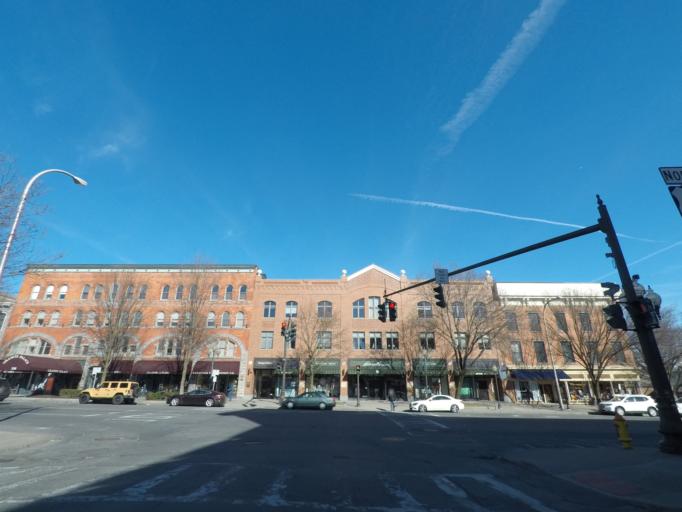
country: US
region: New York
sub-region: Saratoga County
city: Saratoga Springs
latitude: 43.0801
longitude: -73.7861
